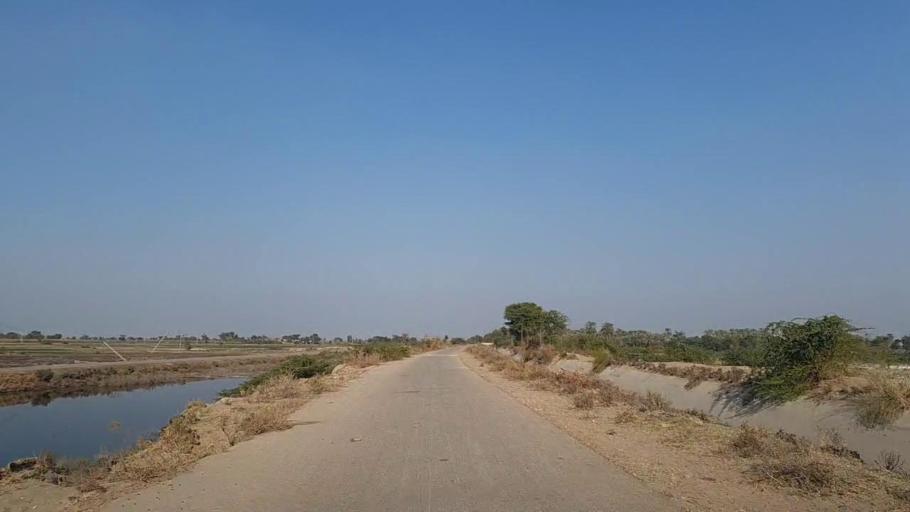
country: PK
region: Sindh
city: Daur
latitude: 26.4315
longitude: 68.2672
